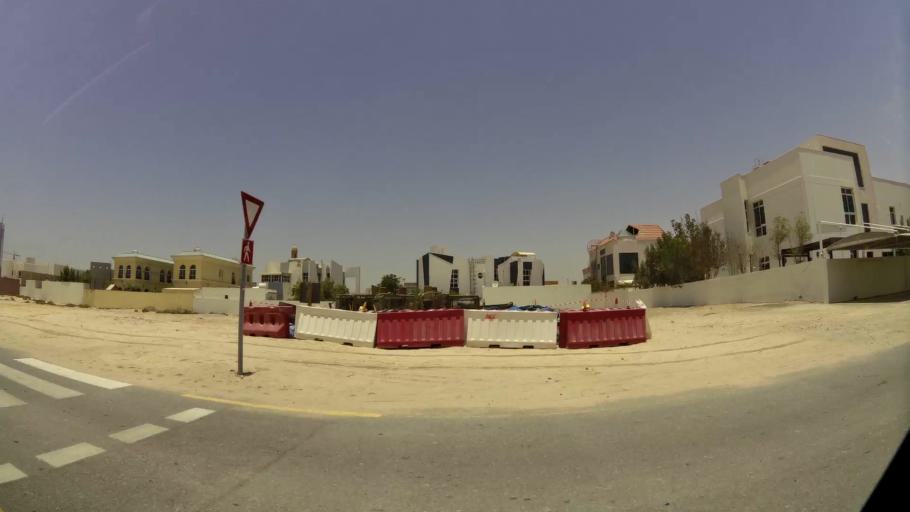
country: AE
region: Dubai
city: Dubai
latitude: 25.0976
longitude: 55.1860
